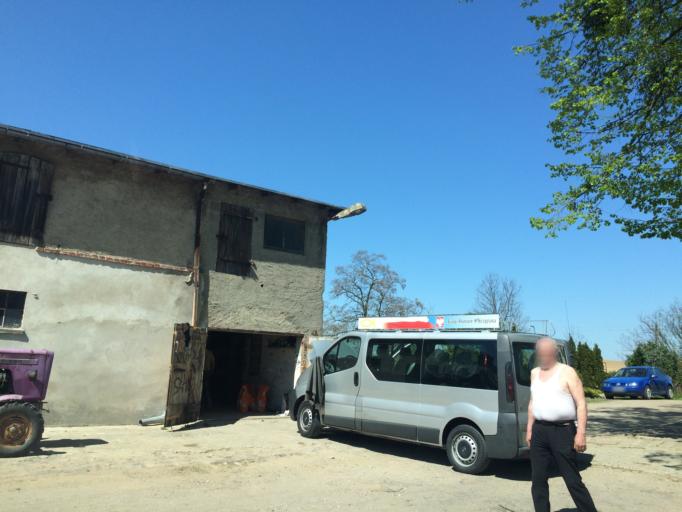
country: PL
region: Warmian-Masurian Voivodeship
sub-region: Powiat nowomiejski
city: Biskupiec
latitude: 53.4709
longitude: 19.2782
